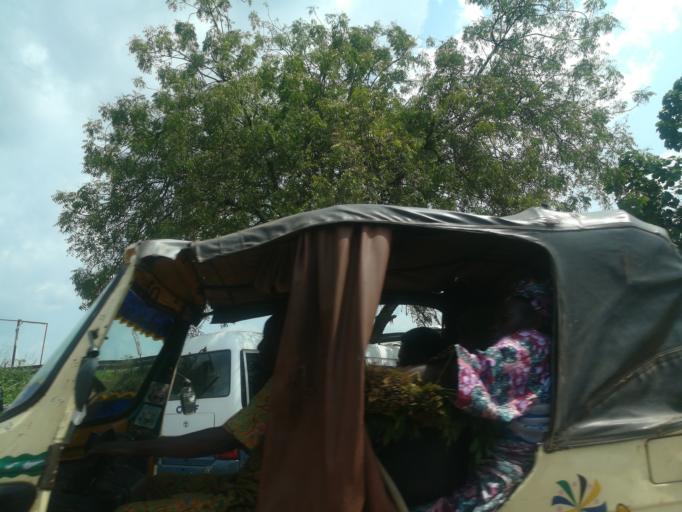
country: NG
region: Oyo
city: Ibadan
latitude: 7.4246
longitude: 3.9369
